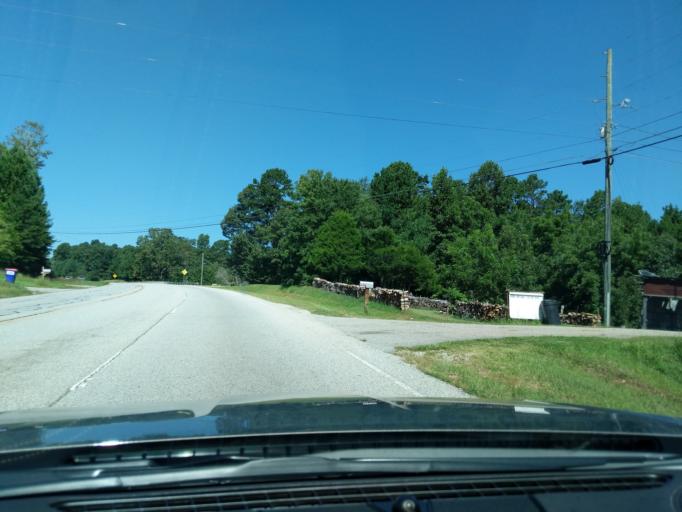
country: US
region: Georgia
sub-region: Habersham County
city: Demorest
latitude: 34.5769
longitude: -83.5971
